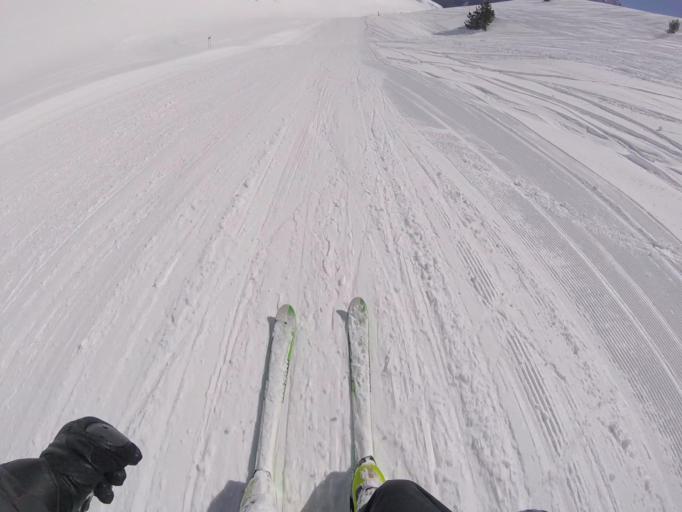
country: ES
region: Catalonia
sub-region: Provincia de Lleida
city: Espot
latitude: 42.6577
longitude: 0.9936
